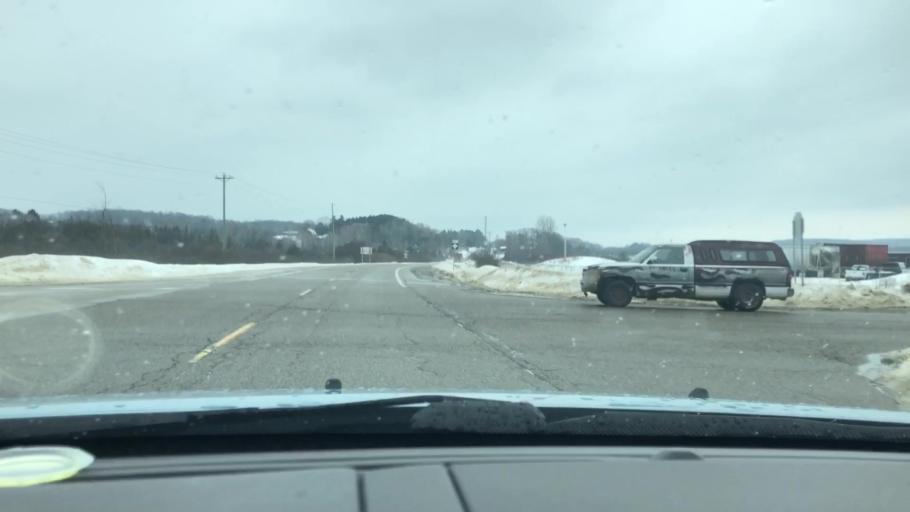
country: US
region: Michigan
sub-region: Charlevoix County
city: East Jordan
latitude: 45.1324
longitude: -85.1395
